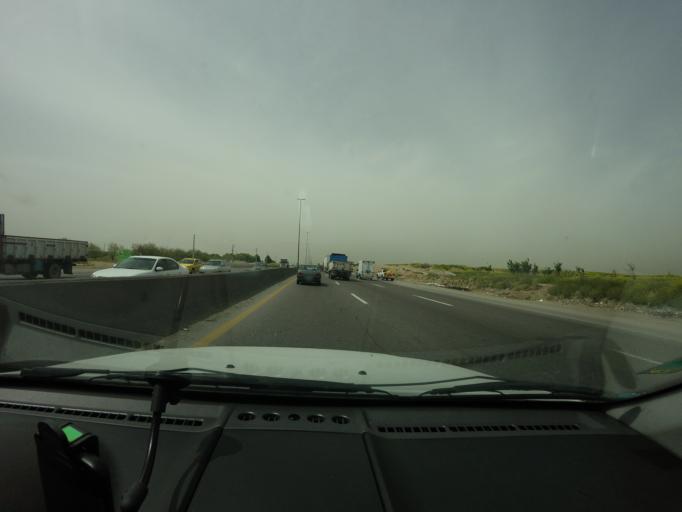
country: IR
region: Tehran
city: Eslamshahr
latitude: 35.5939
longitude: 51.1778
